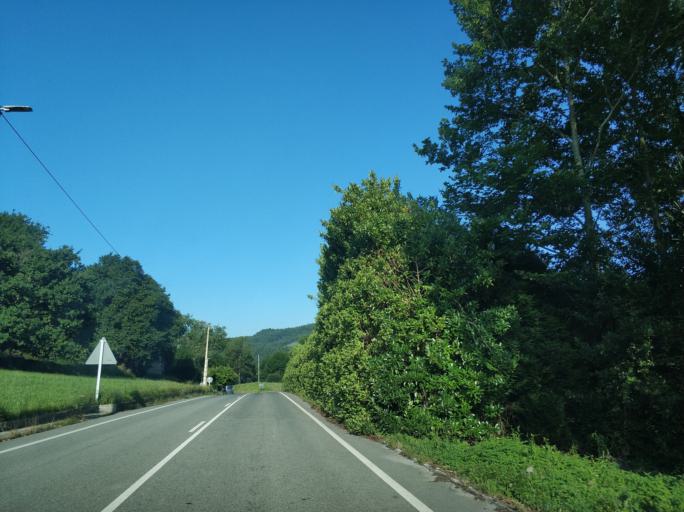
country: ES
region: Cantabria
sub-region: Provincia de Cantabria
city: Miengo
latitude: 43.3880
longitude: -3.9595
